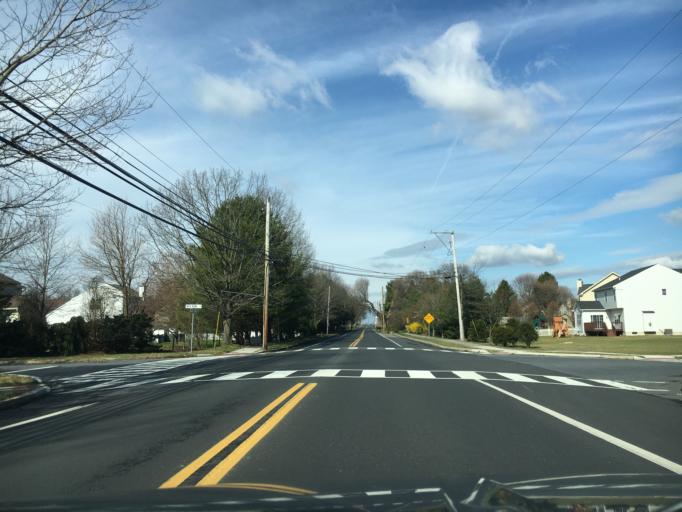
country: US
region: Pennsylvania
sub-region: Northampton County
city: Bath
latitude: 40.6819
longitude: -75.4047
